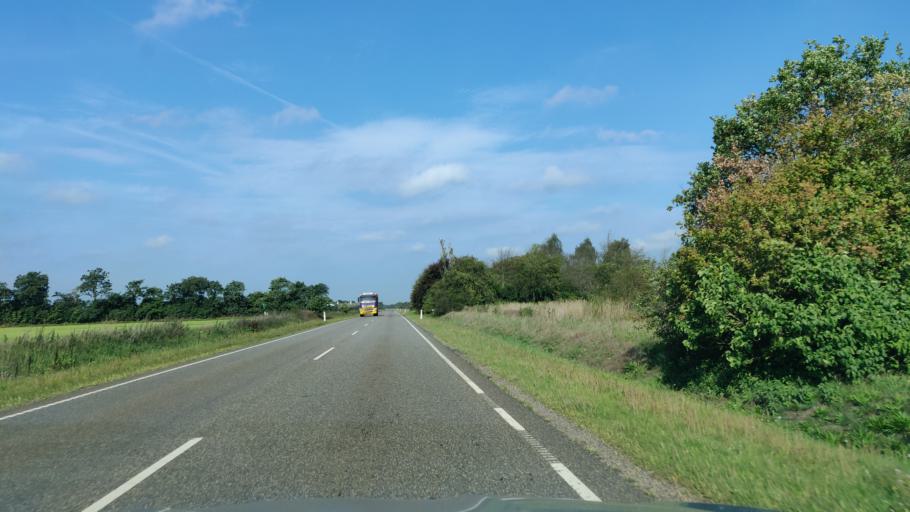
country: DK
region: Central Jutland
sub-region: Herning Kommune
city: Sunds
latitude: 56.2569
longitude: 9.0414
